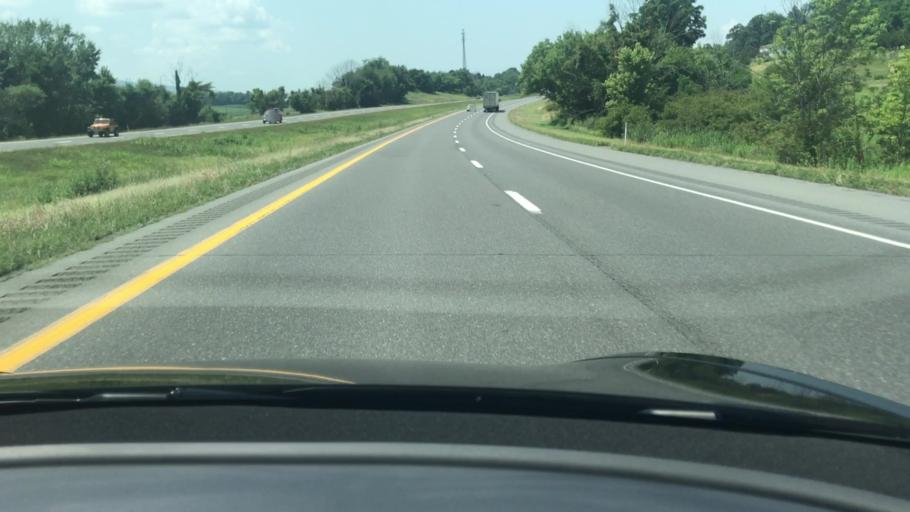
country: US
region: Pennsylvania
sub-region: Juniata County
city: Mifflintown
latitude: 40.5466
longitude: -77.3158
